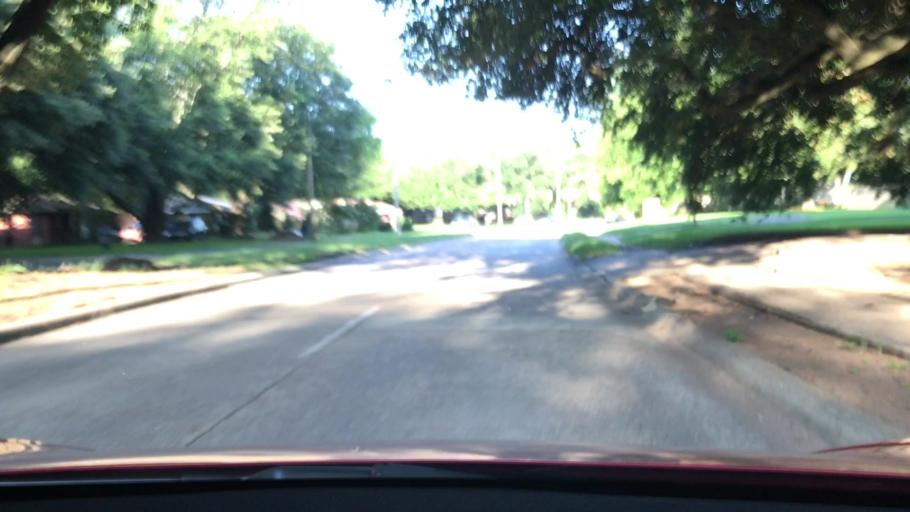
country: US
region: Louisiana
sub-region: Bossier Parish
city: Bossier City
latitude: 32.4552
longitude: -93.7317
